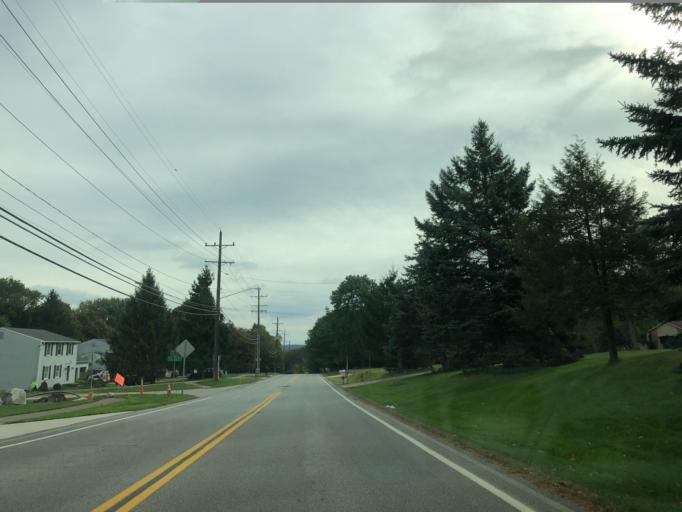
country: US
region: Ohio
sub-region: Cuyahoga County
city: Brecksville
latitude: 41.2830
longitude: -81.6037
